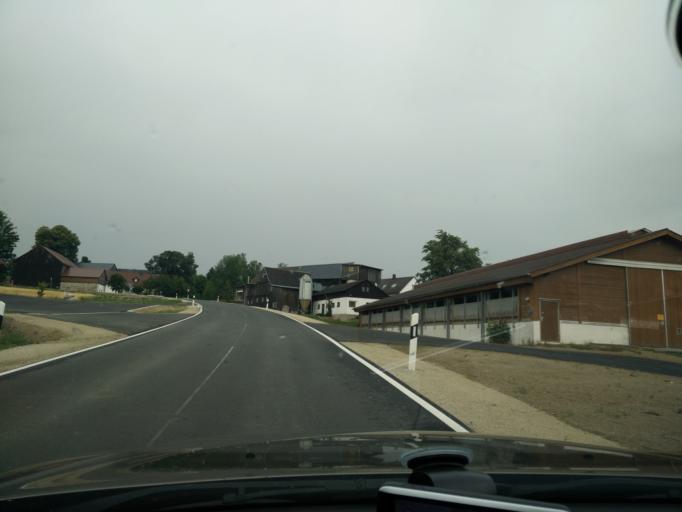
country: DE
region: Bavaria
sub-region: Upper Franconia
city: Trostau
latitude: 50.0490
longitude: 11.9244
